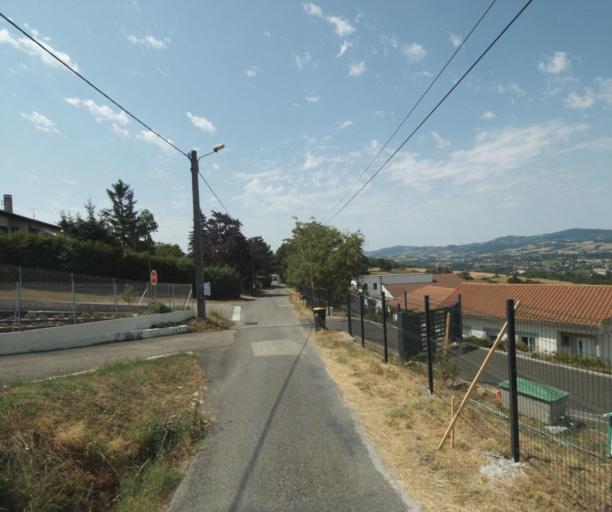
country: FR
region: Rhone-Alpes
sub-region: Departement du Rhone
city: Lentilly
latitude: 45.8363
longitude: 4.6414
